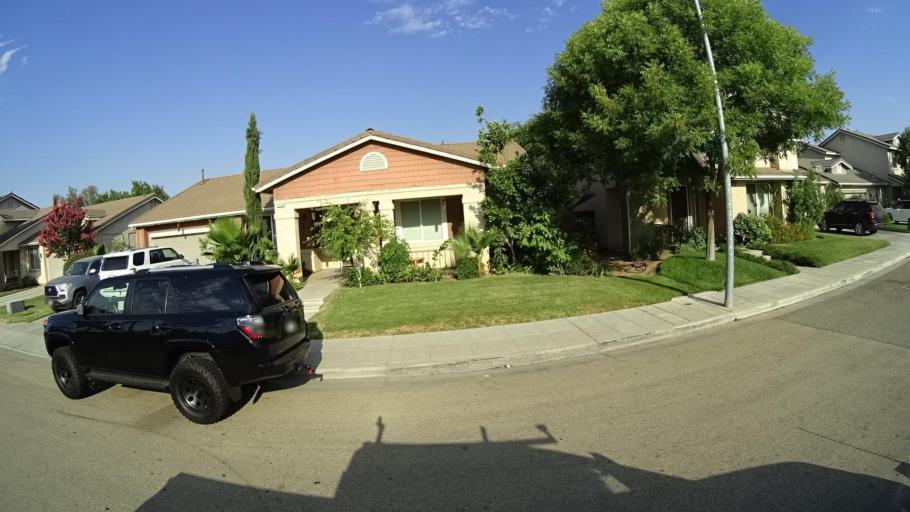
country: US
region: California
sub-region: Fresno County
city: Sunnyside
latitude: 36.7102
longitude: -119.6928
